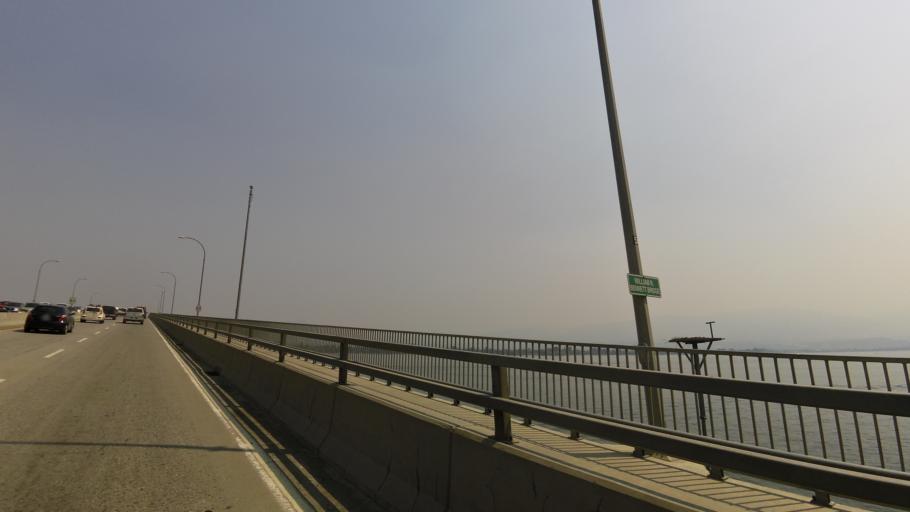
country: CA
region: British Columbia
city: Kelowna
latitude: 49.8780
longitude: -119.5188
